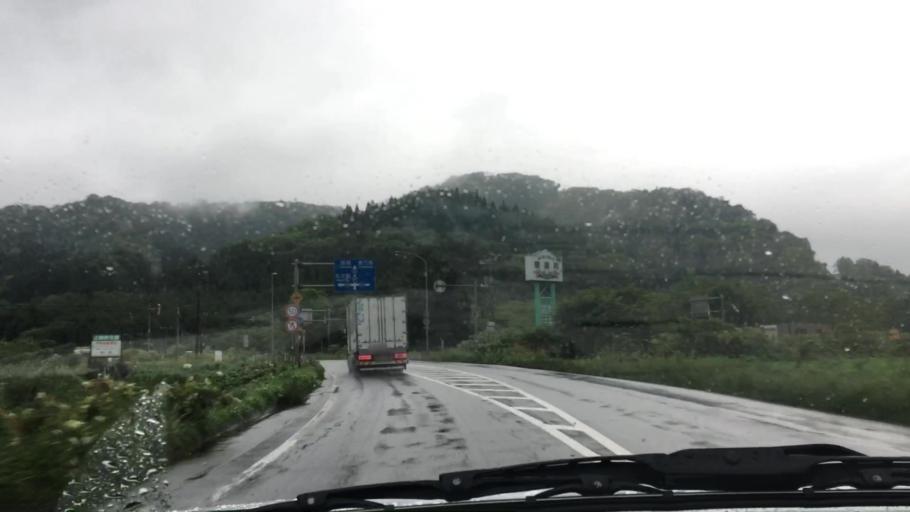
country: JP
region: Hokkaido
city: Niseko Town
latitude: 42.6016
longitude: 140.5853
